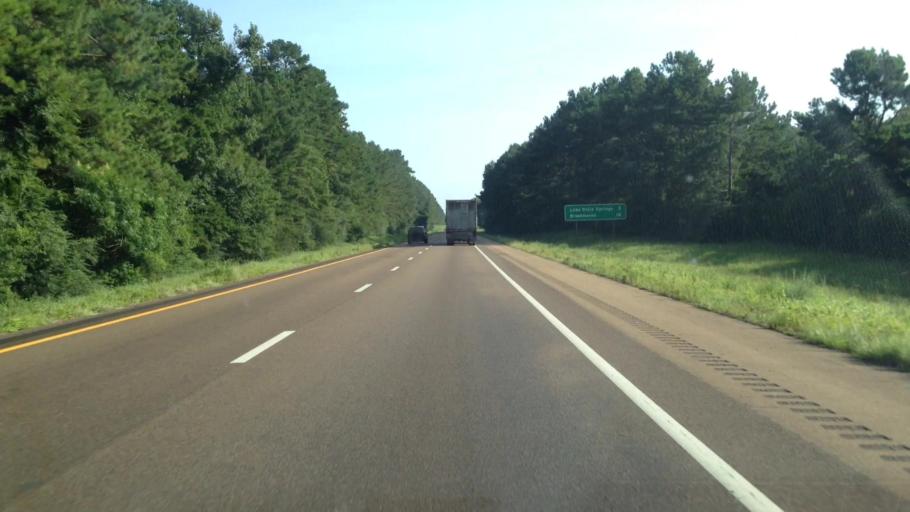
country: US
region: Mississippi
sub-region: Pike County
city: Summit
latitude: 31.3022
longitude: -90.4780
